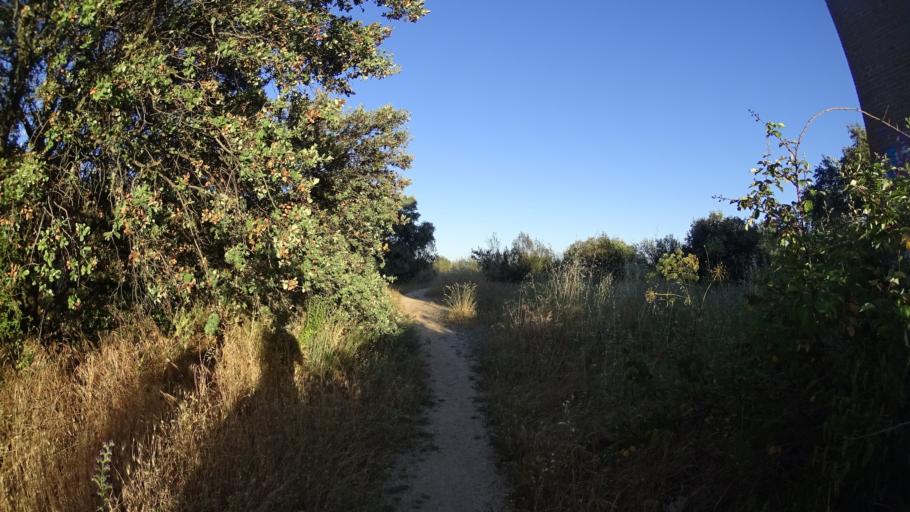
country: ES
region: Madrid
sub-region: Provincia de Madrid
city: Galapagar
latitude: 40.5908
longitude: -3.9701
